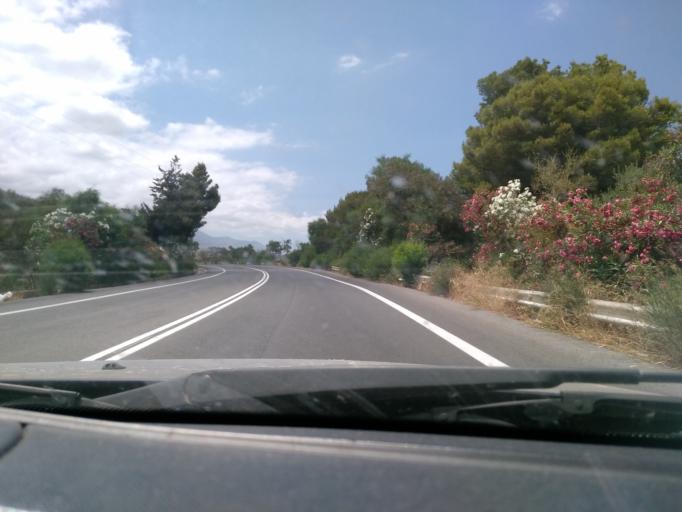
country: GR
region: Crete
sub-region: Nomos Chanias
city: Georgioupolis
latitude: 35.3658
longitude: 24.2325
